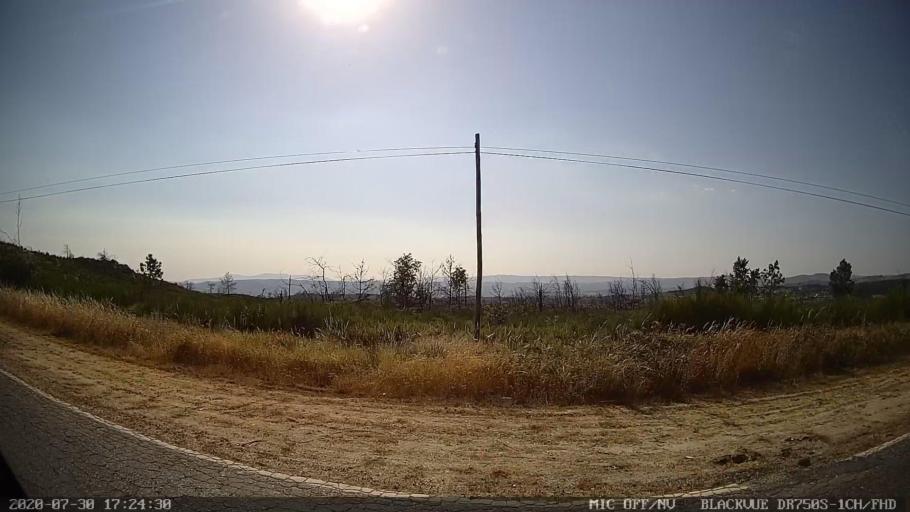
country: PT
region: Vila Real
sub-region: Murca
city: Murca
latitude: 41.3119
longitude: -7.4708
